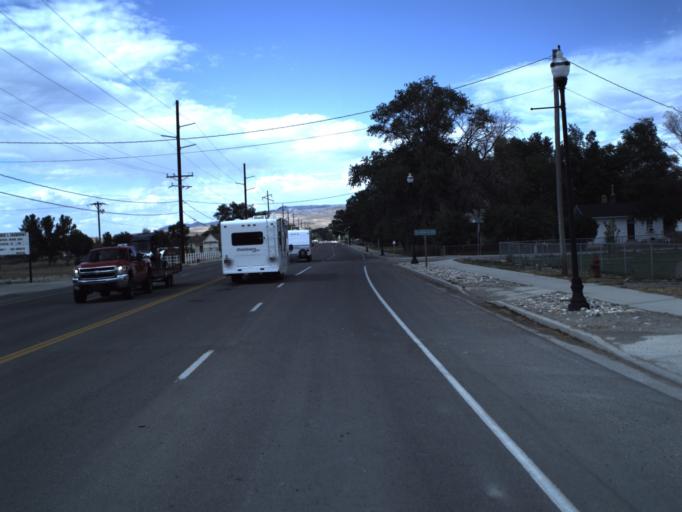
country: US
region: Utah
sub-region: Sanpete County
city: Centerfield
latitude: 39.1374
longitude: -111.8189
